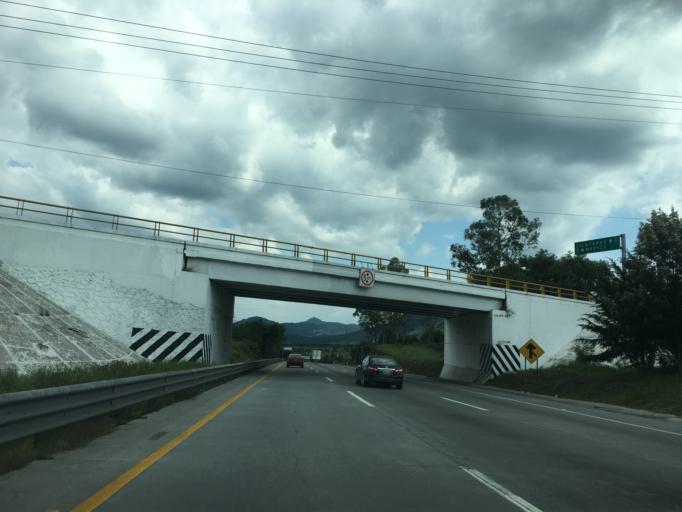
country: MX
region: Hidalgo
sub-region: Tepeji del Rio de Ocampo
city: Santiago Tlautla
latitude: 19.9816
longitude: -99.4395
